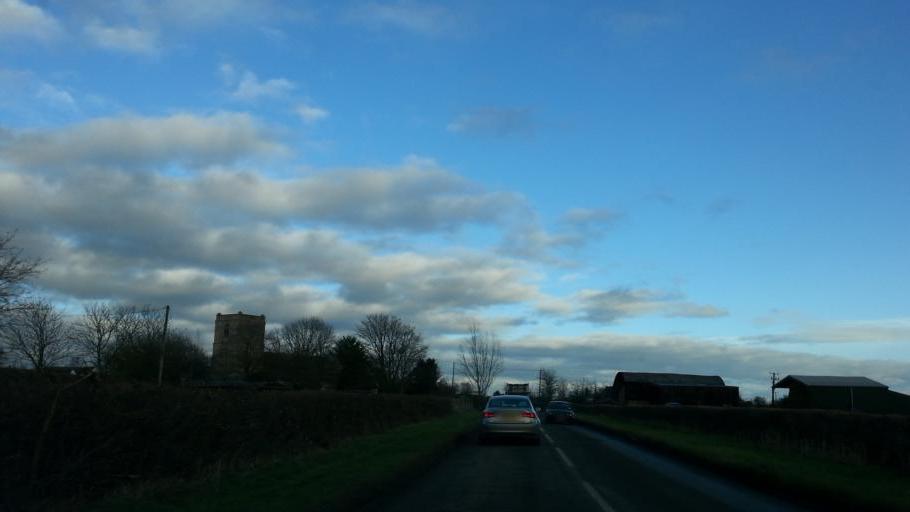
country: GB
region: England
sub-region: Oxfordshire
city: Faringdon
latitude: 51.6137
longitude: -1.6071
